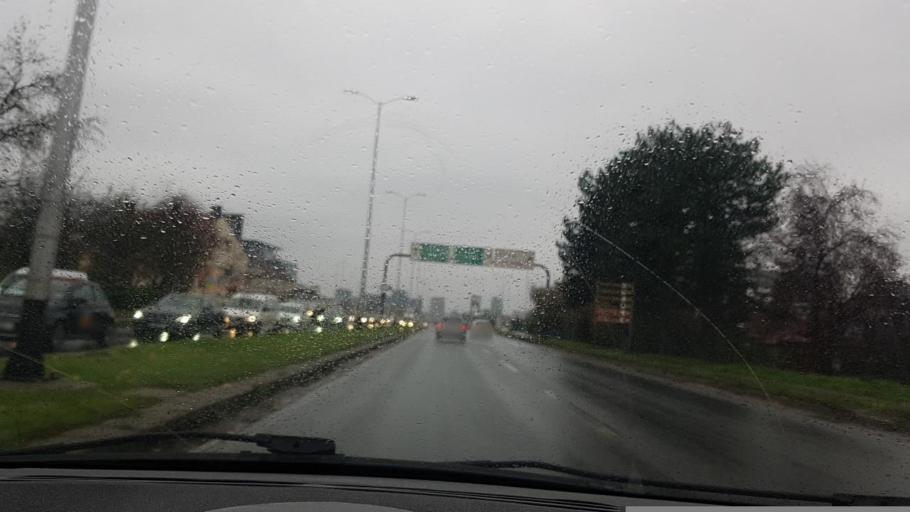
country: HR
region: Grad Zagreb
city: Novi Zagreb
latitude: 45.7940
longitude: 15.9843
